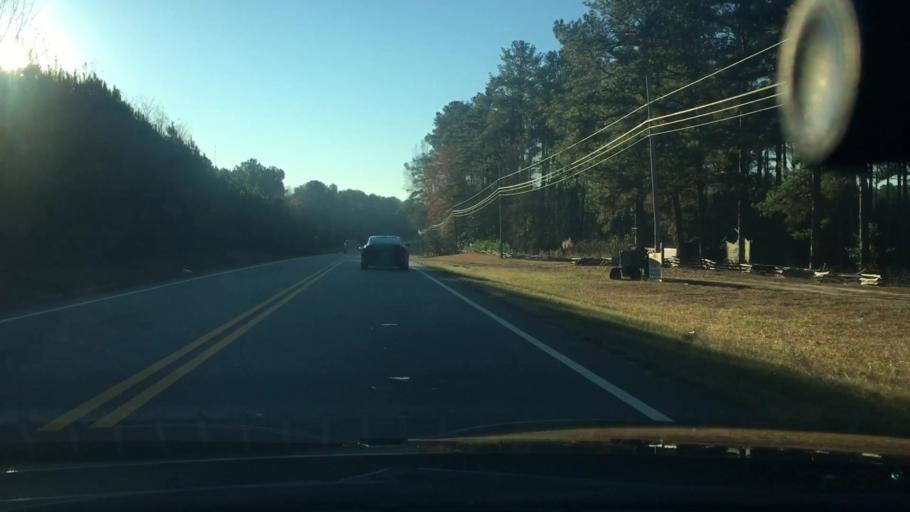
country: US
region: Georgia
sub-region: Coweta County
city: Senoia
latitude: 33.2893
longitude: -84.5408
